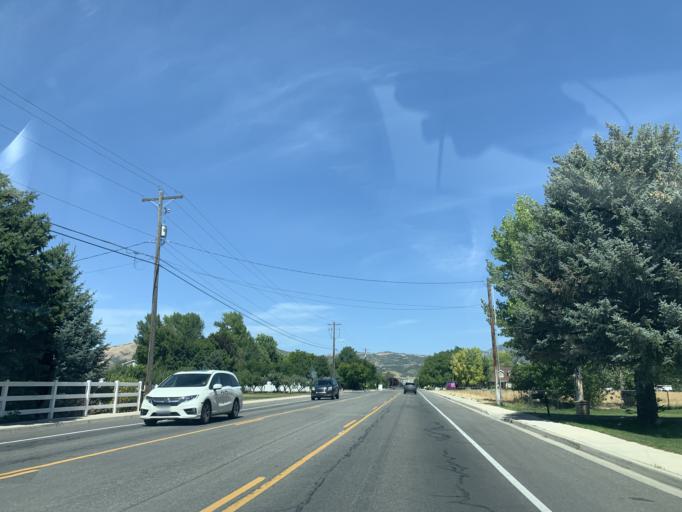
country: US
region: Utah
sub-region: Utah County
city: Lehi
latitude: 40.4104
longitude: -111.8302
